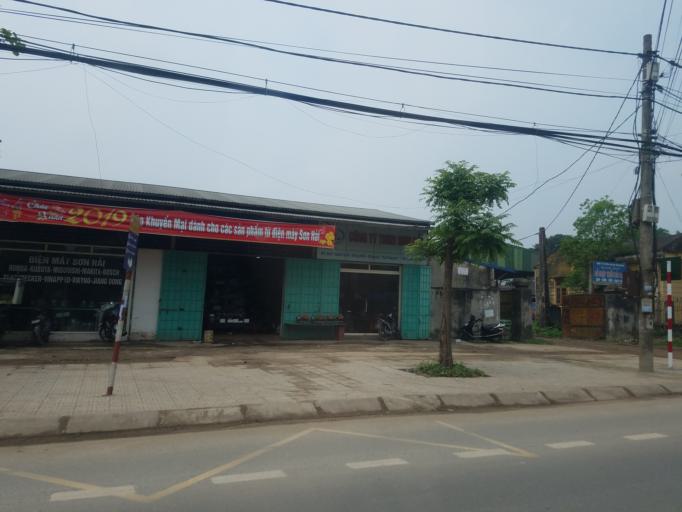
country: VN
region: Thai Nguyen
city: Chua Hang
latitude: 21.6102
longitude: 105.8396
